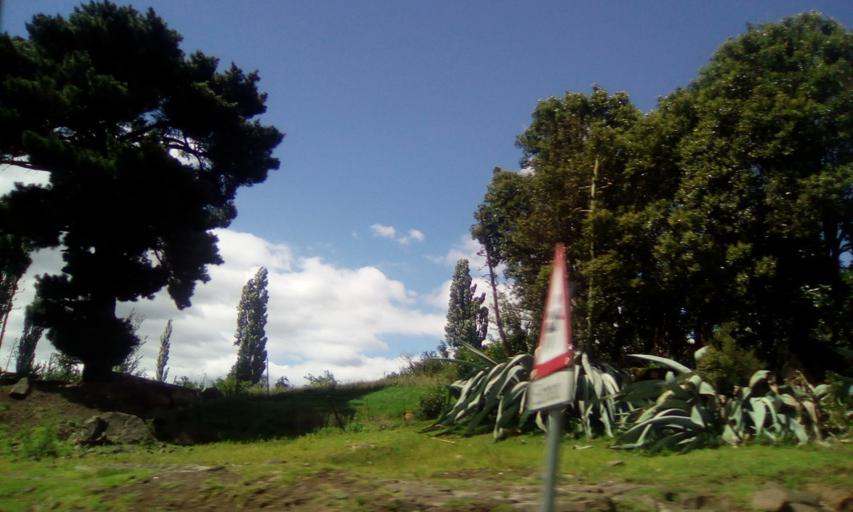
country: LS
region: Maseru
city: Nako
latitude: -29.6621
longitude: 27.7893
